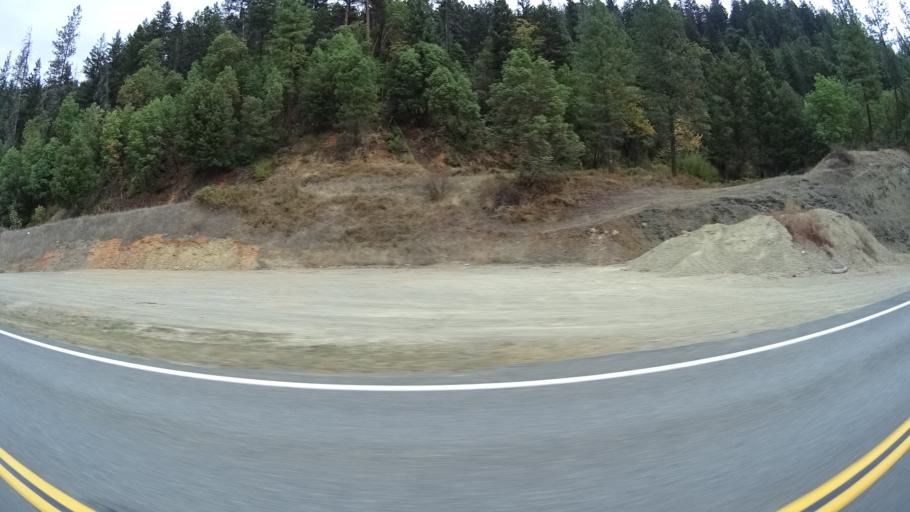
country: US
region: California
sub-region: Siskiyou County
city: Happy Camp
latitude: 41.8107
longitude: -123.3531
